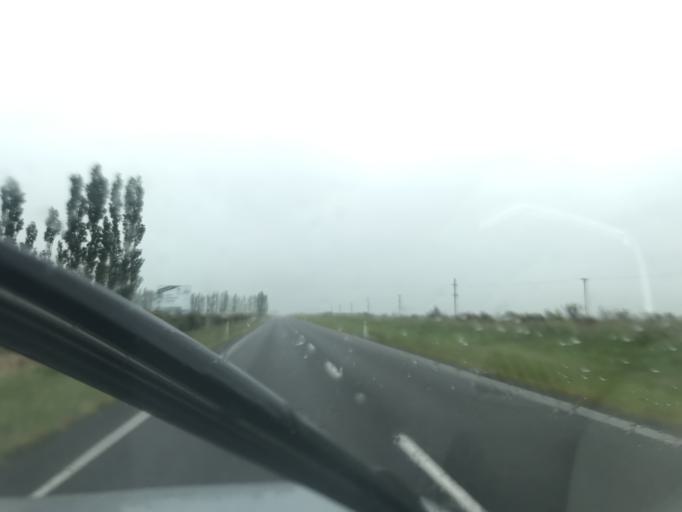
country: NZ
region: Canterbury
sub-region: Selwyn District
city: Darfield
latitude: -43.5038
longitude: 172.2218
